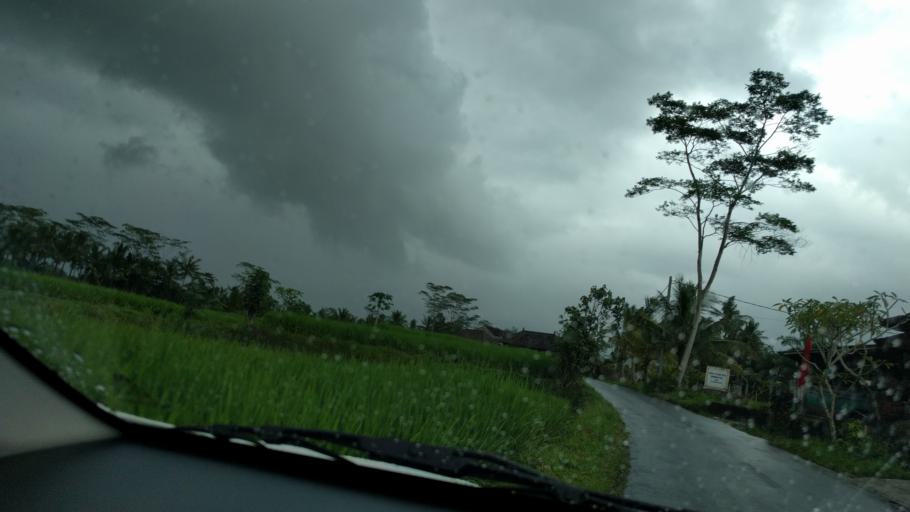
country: ID
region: Bali
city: Banjar Triwangsakeliki
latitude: -8.4633
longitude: 115.2597
